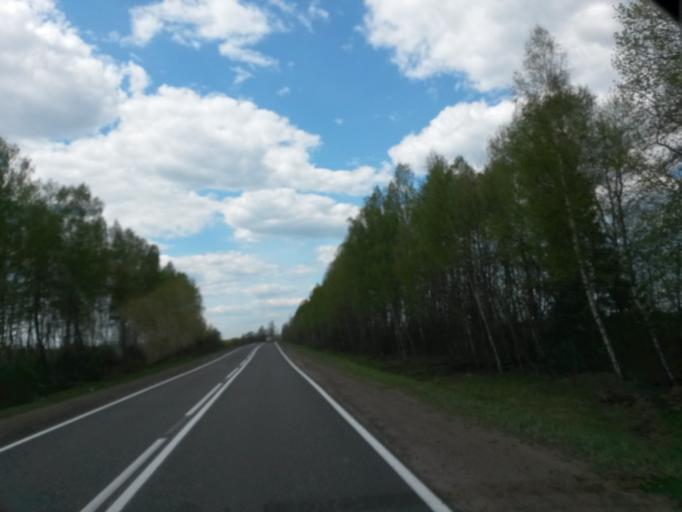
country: RU
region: Jaroslavl
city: Bol'shoye Selo
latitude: 57.7148
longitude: 39.1345
